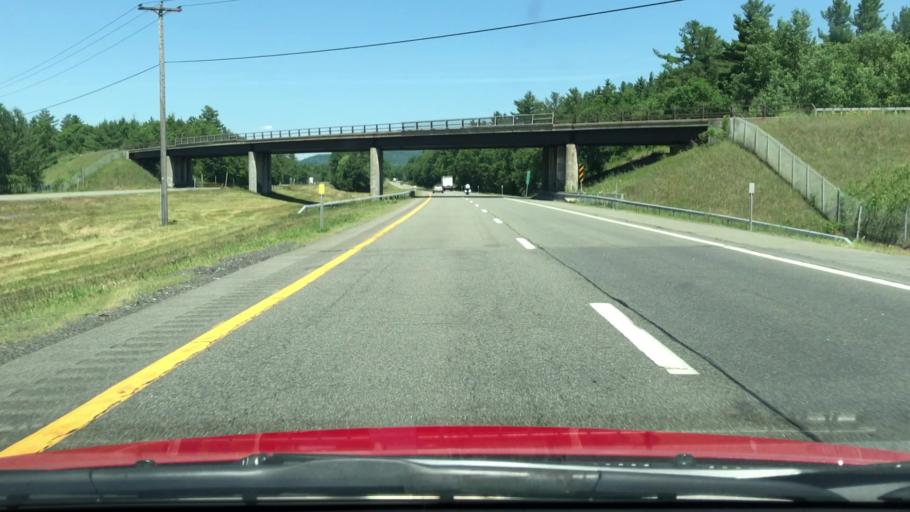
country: US
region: New York
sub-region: Essex County
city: Elizabethtown
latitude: 44.3253
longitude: -73.5292
